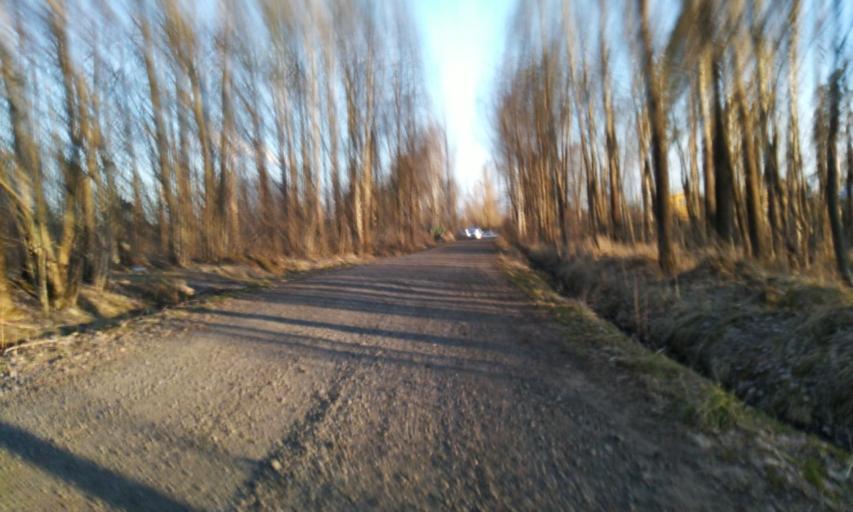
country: RU
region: Leningrad
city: Novoye Devyatkino
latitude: 60.0870
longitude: 30.4577
